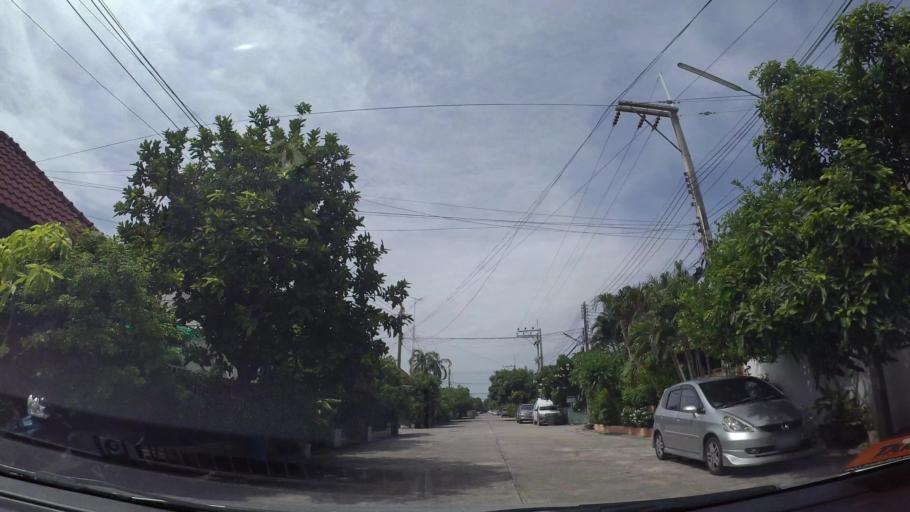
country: TH
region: Chon Buri
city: Chon Buri
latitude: 13.3263
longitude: 100.9500
